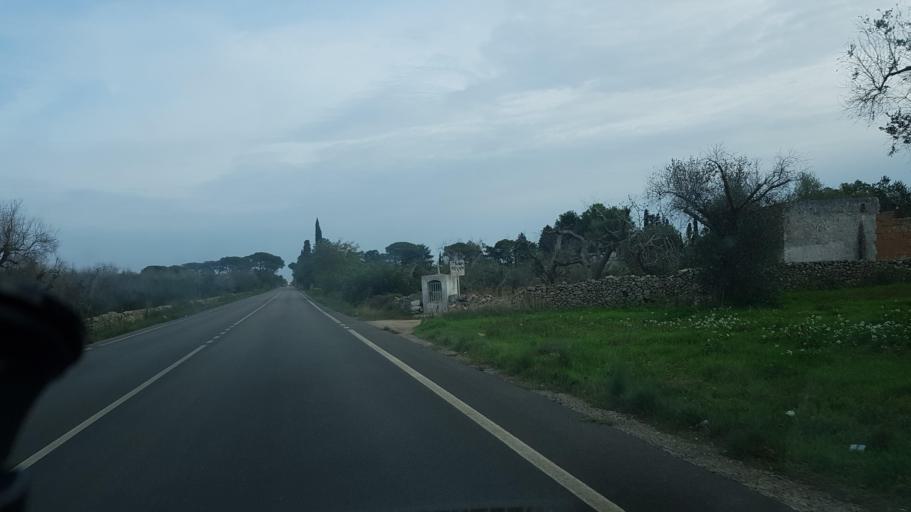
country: IT
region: Apulia
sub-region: Provincia di Lecce
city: Trepuzzi
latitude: 40.3946
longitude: 18.0924
